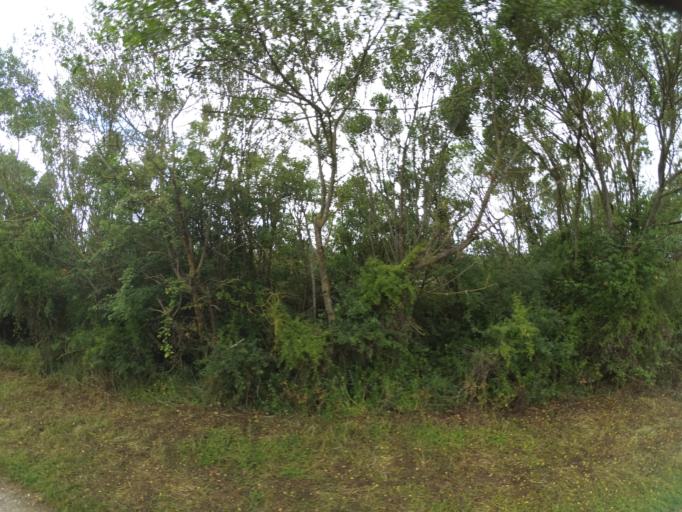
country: FR
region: Poitou-Charentes
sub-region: Departement de la Charente-Maritime
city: Aytre
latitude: 46.1296
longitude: -1.1305
